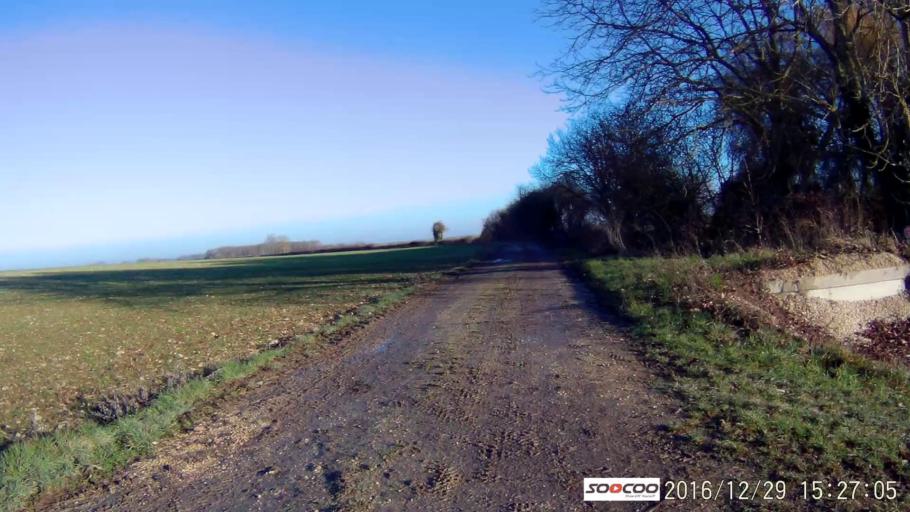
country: FR
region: Centre
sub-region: Departement de l'Indre
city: Neuvy-Pailloux
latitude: 46.9371
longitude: 1.8272
